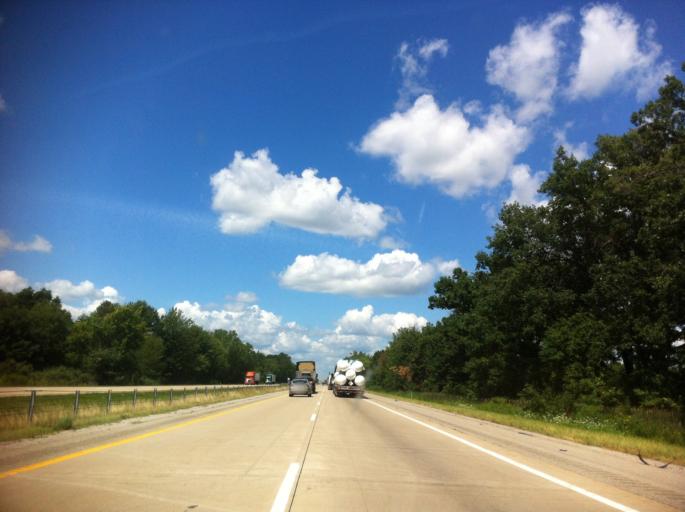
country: US
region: Michigan
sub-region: Monroe County
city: Petersburg
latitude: 41.8745
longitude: -83.6610
